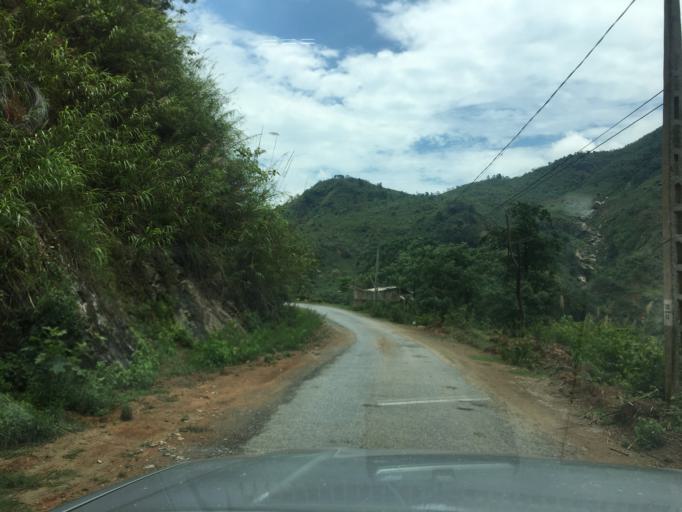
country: VN
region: Yen Bai
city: Son Thinh
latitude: 21.6791
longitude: 104.5541
